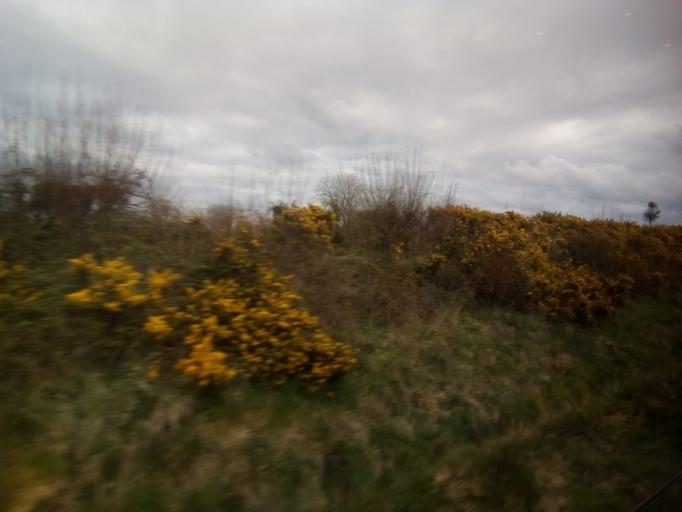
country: IE
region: Leinster
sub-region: An Longfort
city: Longford
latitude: 53.7145
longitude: -7.7511
